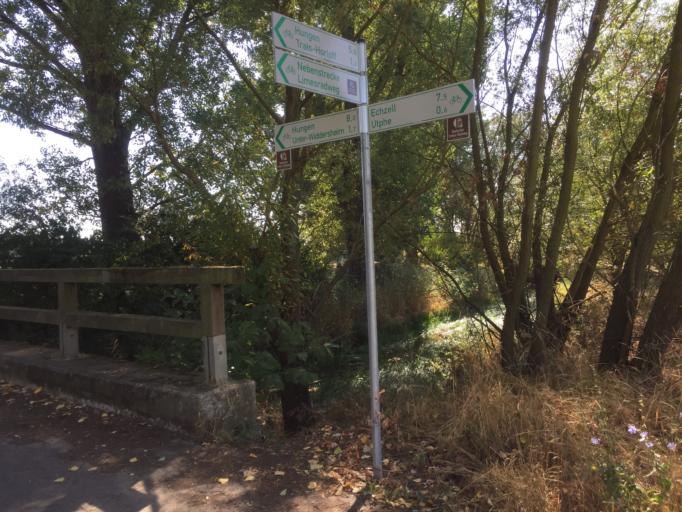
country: DE
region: Hesse
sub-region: Regierungsbezirk Giessen
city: Hungen
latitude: 50.4355
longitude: 8.8966
